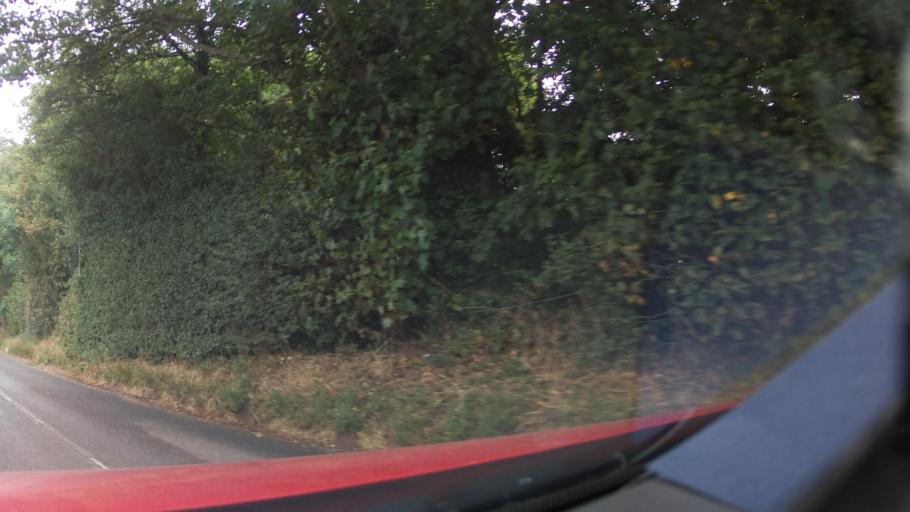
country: GB
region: England
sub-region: Shropshire
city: Woodcote
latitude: 52.7041
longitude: -2.3555
